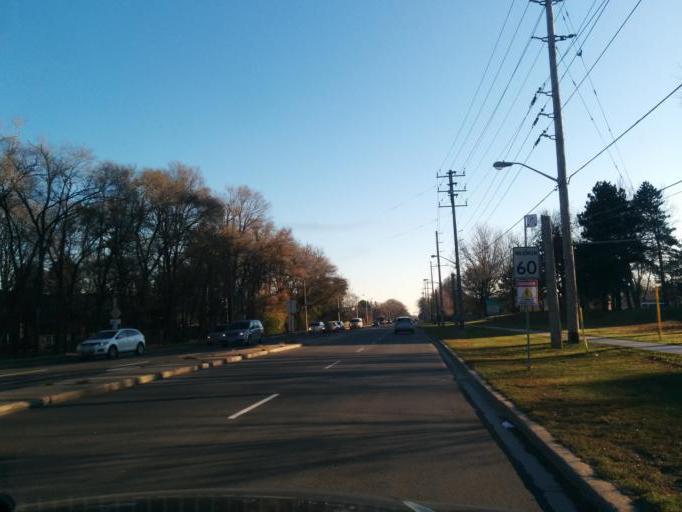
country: CA
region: Ontario
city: Etobicoke
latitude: 43.6770
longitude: -79.5510
